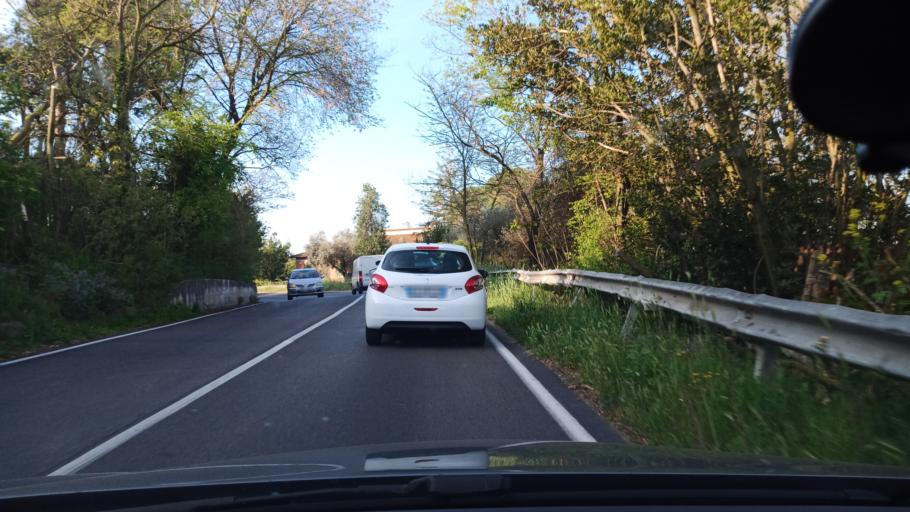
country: IT
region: Latium
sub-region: Citta metropolitana di Roma Capitale
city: Fiano Romano
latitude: 42.1720
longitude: 12.6355
